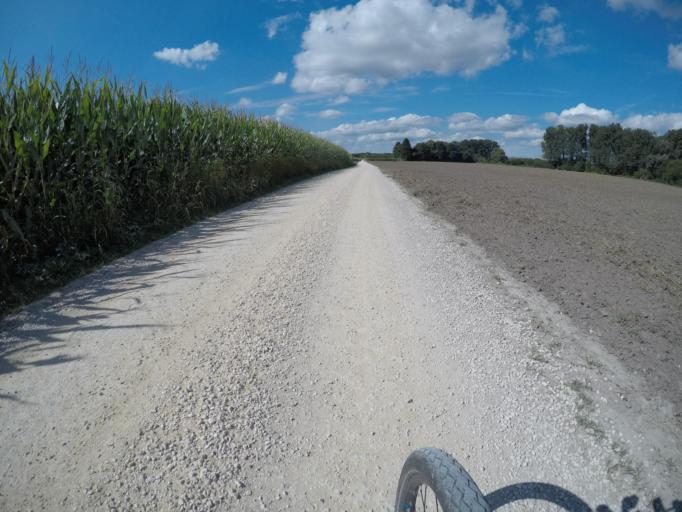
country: DE
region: Bavaria
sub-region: Swabia
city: Wittislingen
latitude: 48.6100
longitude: 10.4384
